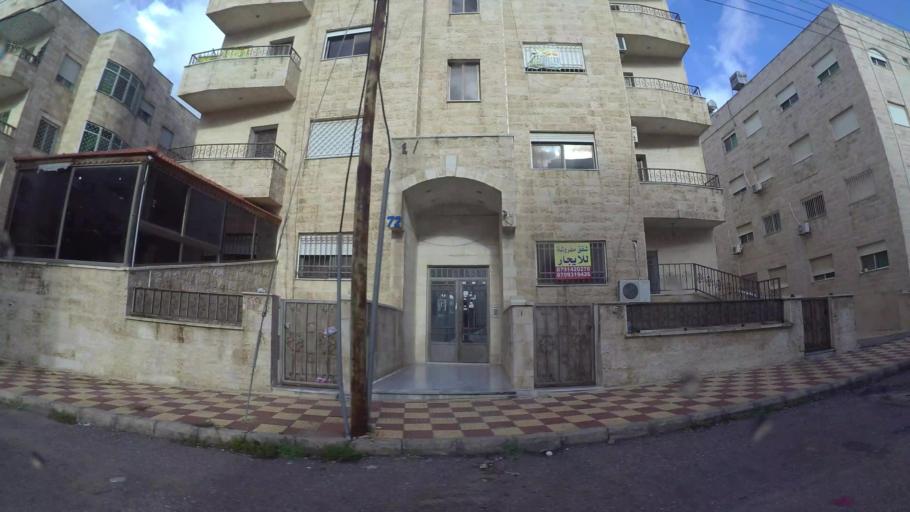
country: JO
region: Amman
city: Al Jubayhah
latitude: 32.0302
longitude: 35.8703
